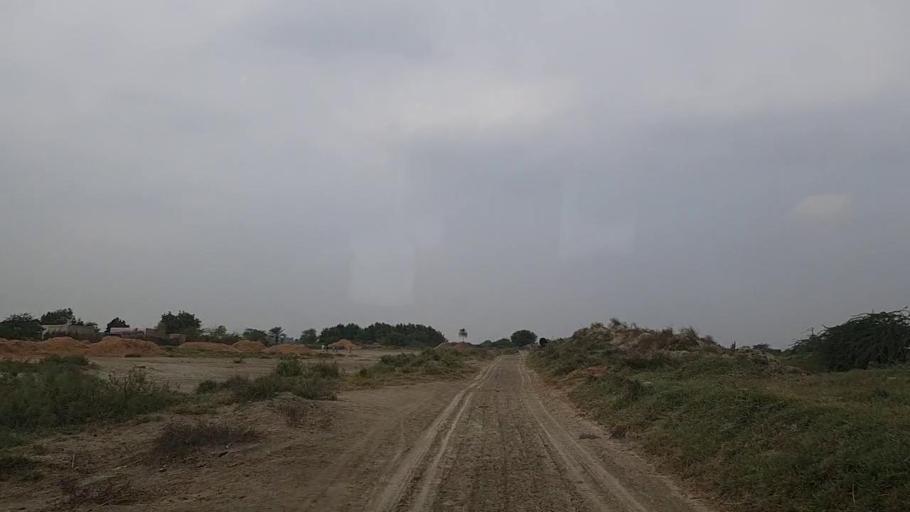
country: PK
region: Sindh
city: Mirpur Sakro
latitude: 24.5922
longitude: 67.7000
